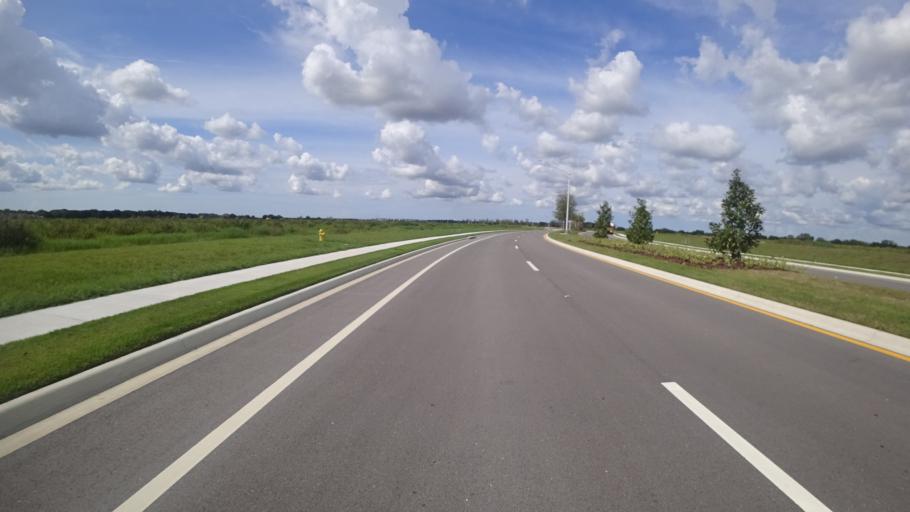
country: US
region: Florida
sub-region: Sarasota County
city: The Meadows
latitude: 27.4493
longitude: -82.3557
